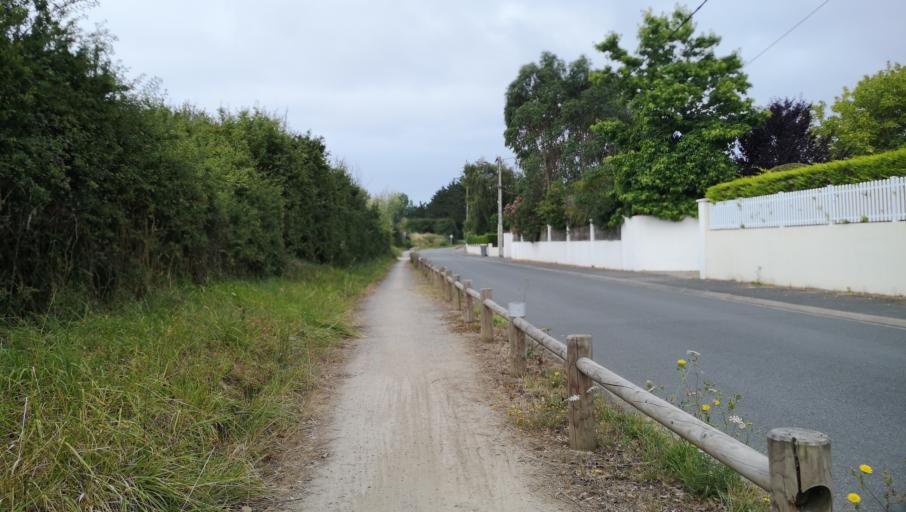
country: FR
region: Pays de la Loire
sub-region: Departement de la Vendee
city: Olonne-sur-Mer
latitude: 46.5293
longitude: -1.7955
